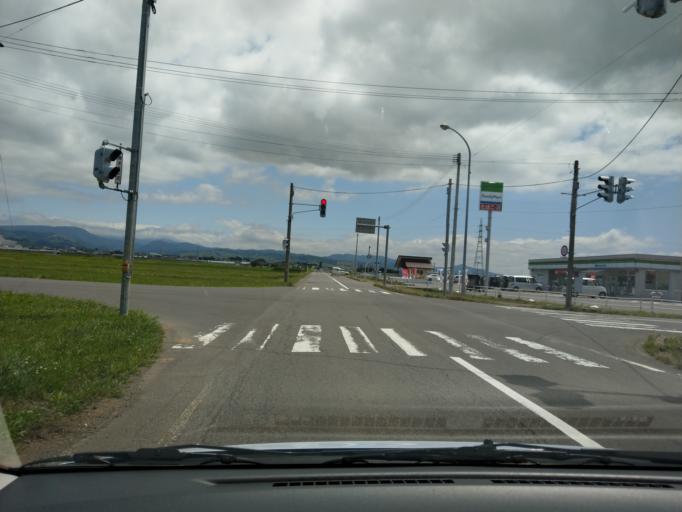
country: JP
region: Aomori
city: Kuroishi
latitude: 40.6590
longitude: 140.5620
